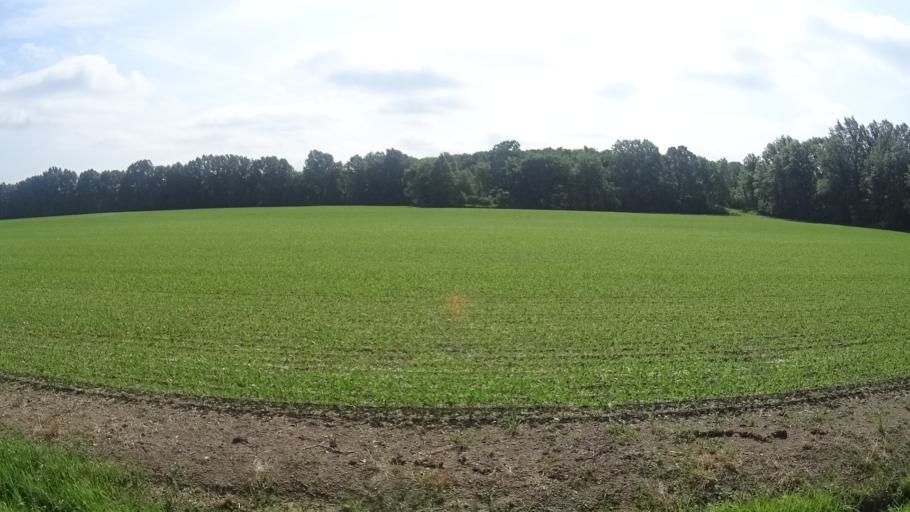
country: US
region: Ohio
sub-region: Lorain County
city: Vermilion
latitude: 41.3801
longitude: -82.4184
